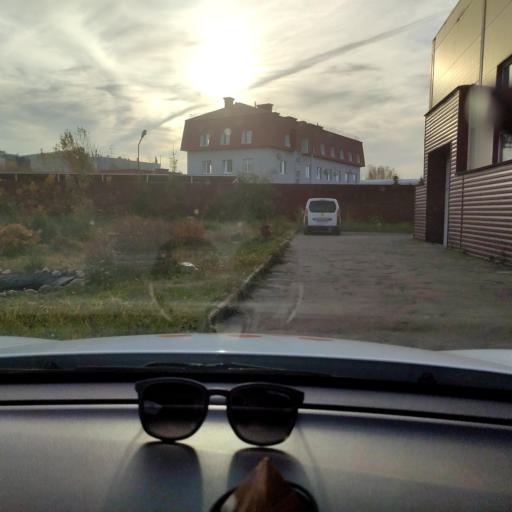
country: RU
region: Tatarstan
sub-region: Gorod Kazan'
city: Kazan
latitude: 55.7694
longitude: 49.0975
